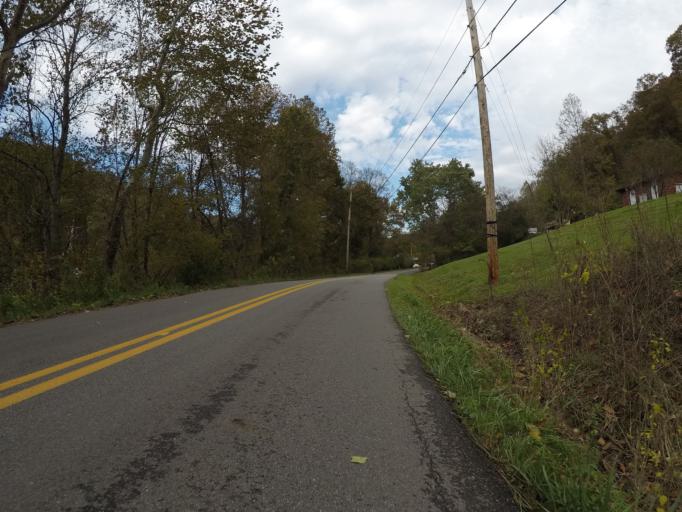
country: US
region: West Virginia
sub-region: Wayne County
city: Lavalette
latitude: 38.3409
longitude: -82.4500
